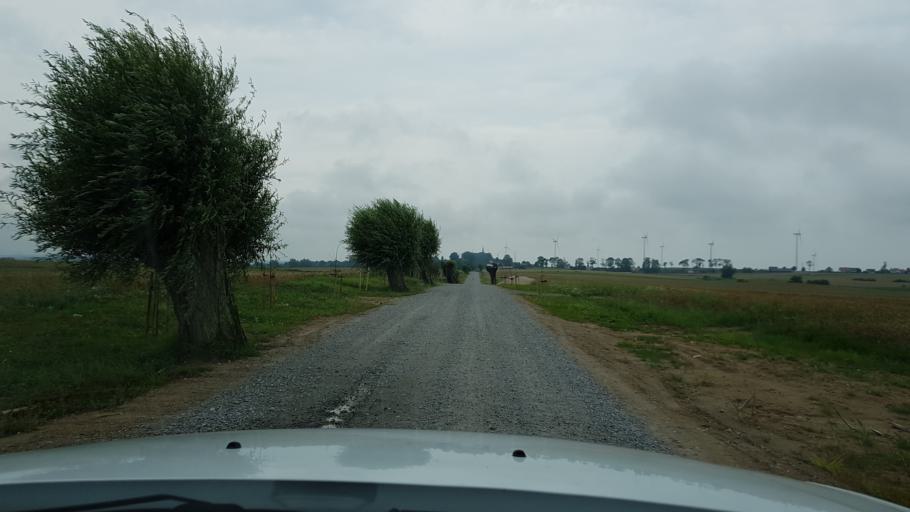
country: PL
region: West Pomeranian Voivodeship
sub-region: Powiat slawienski
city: Darlowo
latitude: 54.4527
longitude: 16.4530
